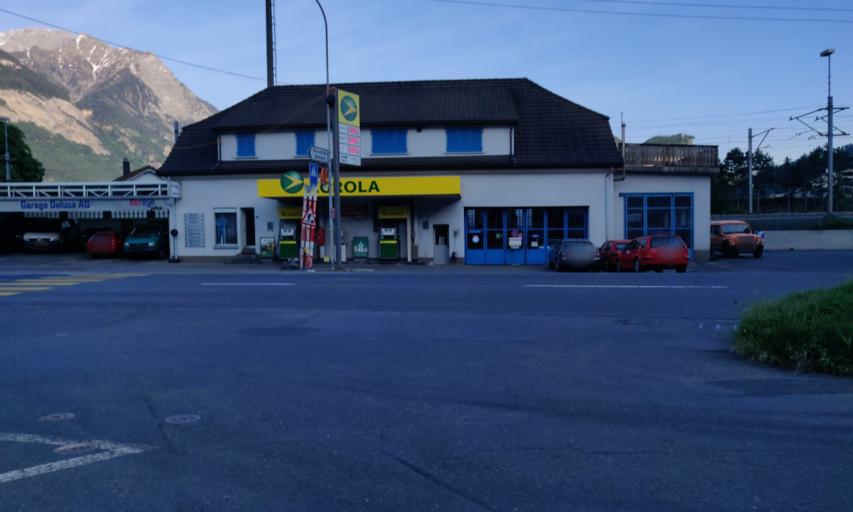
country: LI
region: Balzers
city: Balzers
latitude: 47.0707
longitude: 9.4777
